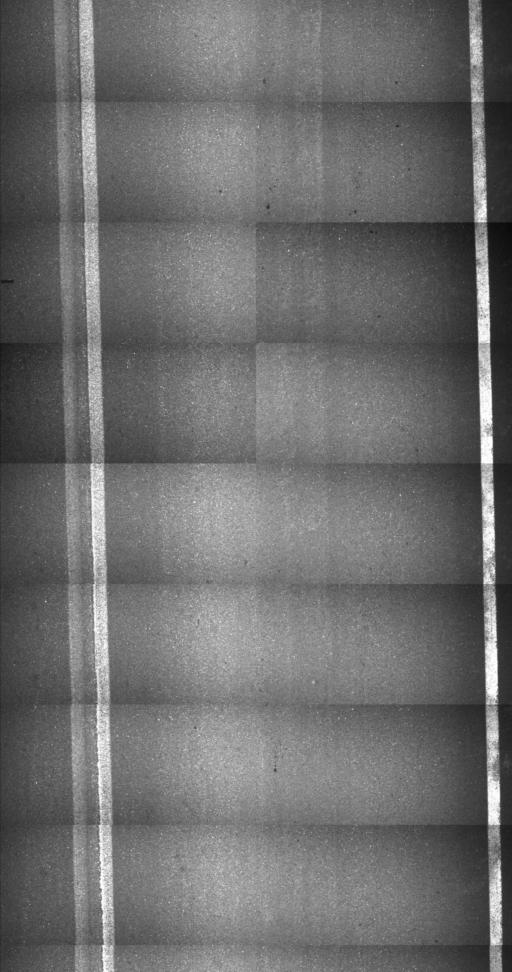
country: US
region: New Hampshire
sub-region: Coos County
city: Colebrook
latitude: 44.9649
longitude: -71.5266
